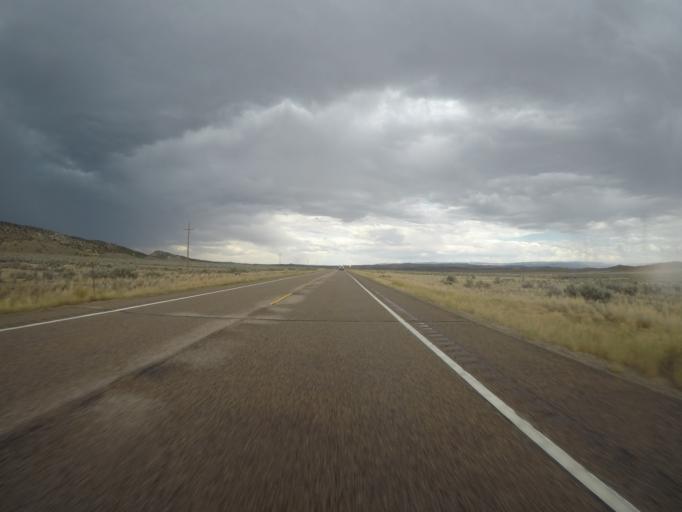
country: US
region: Colorado
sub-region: Rio Blanco County
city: Rangely
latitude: 40.2392
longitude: -108.9212
